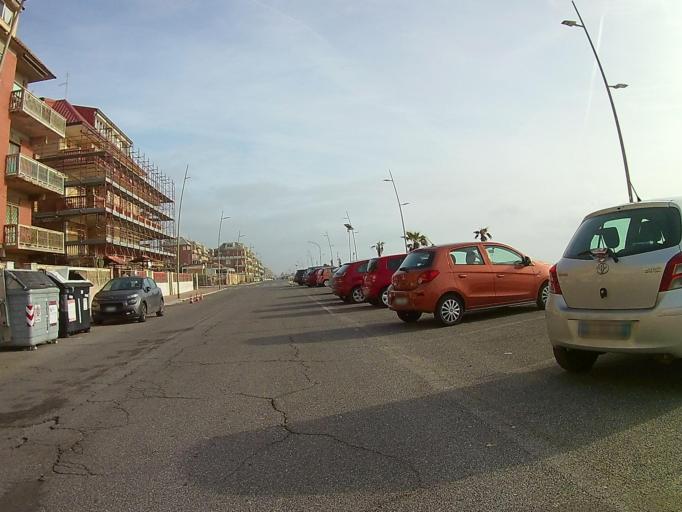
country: IT
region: Latium
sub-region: Citta metropolitana di Roma Capitale
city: Lido di Ostia
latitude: 41.7365
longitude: 12.2557
